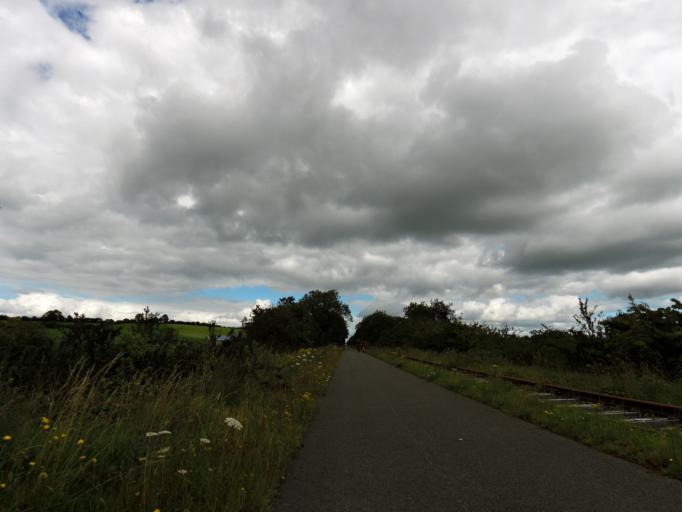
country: IE
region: Leinster
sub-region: An Iarmhi
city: Moate
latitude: 53.4062
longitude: -7.6793
